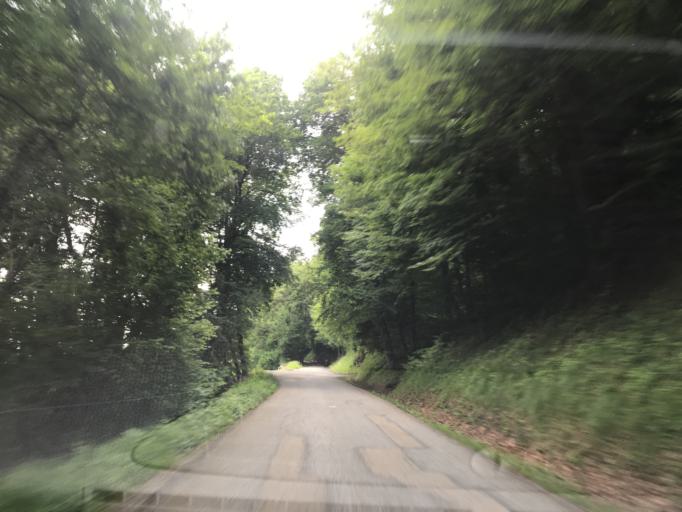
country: FR
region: Rhone-Alpes
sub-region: Departement de la Savoie
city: Mercury
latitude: 45.6793
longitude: 6.3270
